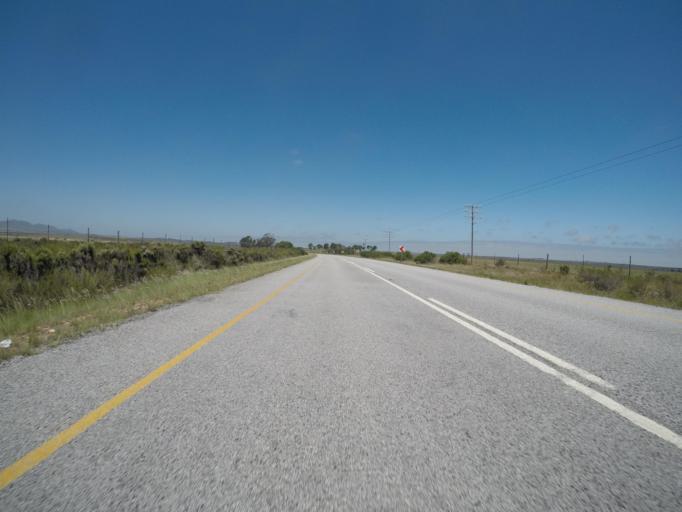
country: ZA
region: Eastern Cape
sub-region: Cacadu District Municipality
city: Kruisfontein
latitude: -34.0165
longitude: 24.5693
